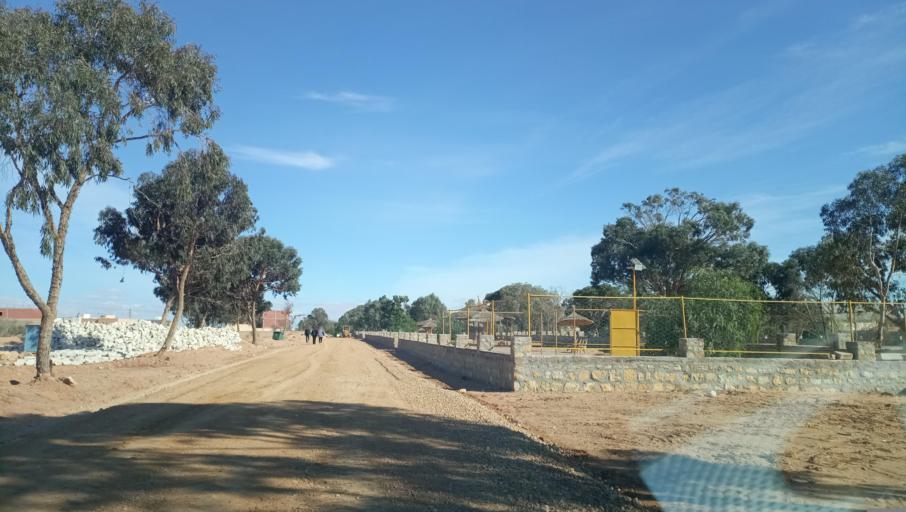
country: TN
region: Madanin
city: Medenine
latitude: 33.1805
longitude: 10.4386
